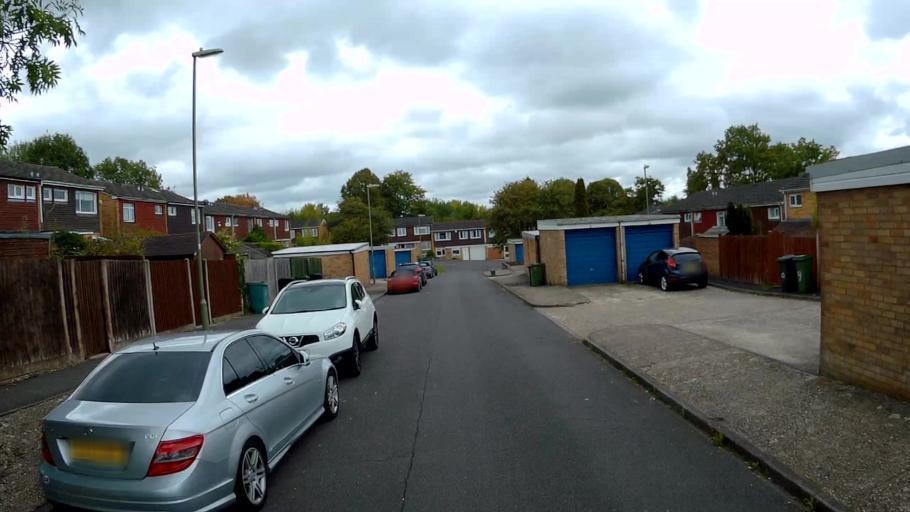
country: GB
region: England
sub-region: Hampshire
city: Basingstoke
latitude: 51.2669
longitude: -1.1253
